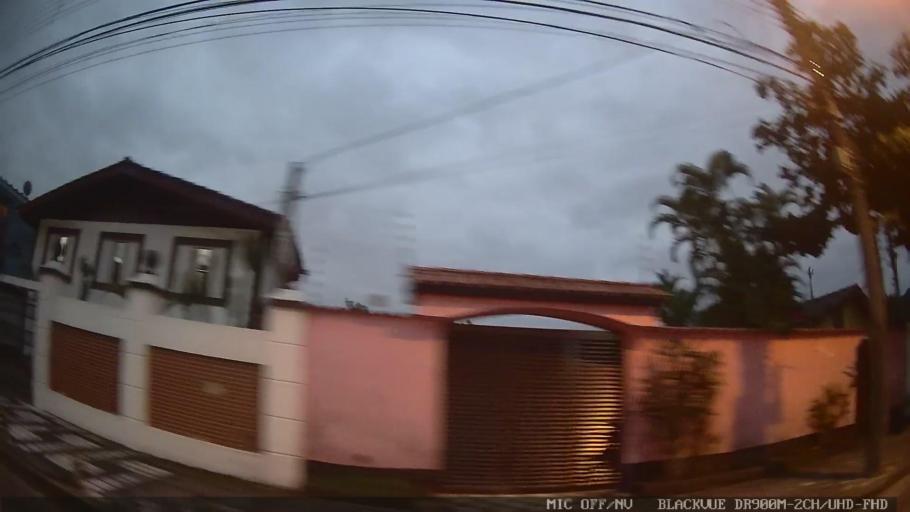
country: BR
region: Sao Paulo
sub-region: Guaruja
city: Guaruja
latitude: -23.9898
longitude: -46.2666
